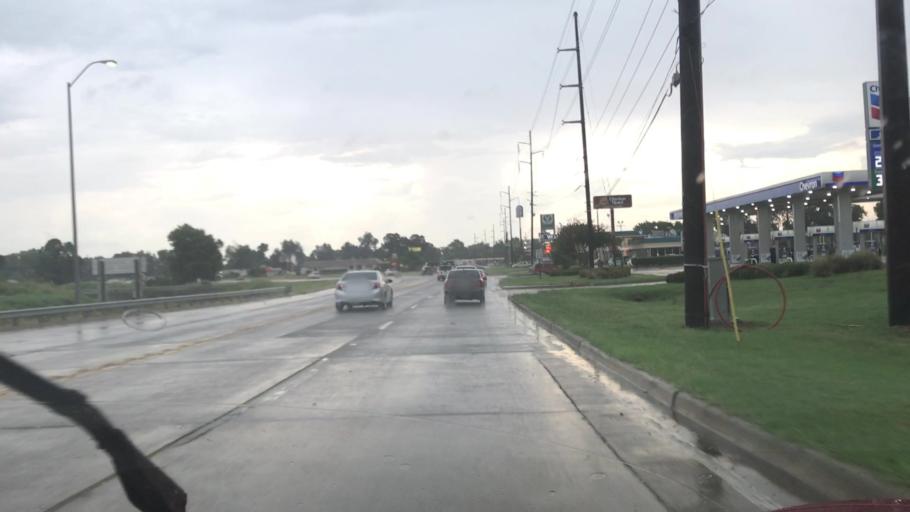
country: US
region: Louisiana
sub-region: Bossier Parish
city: Bossier City
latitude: 32.5296
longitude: -93.6735
